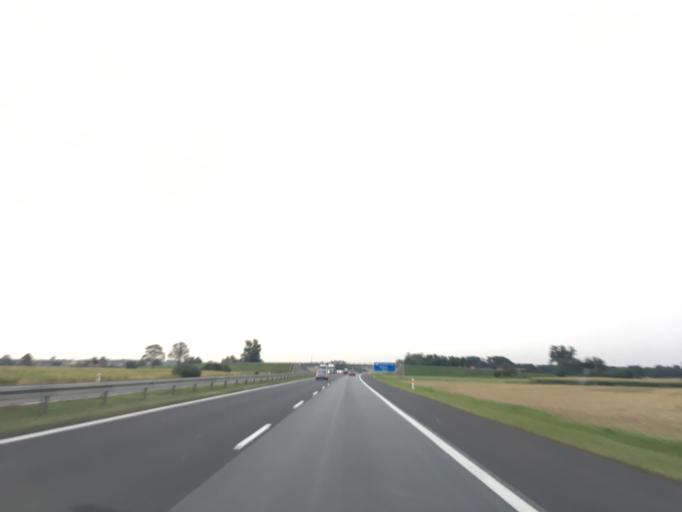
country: PL
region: Lodz Voivodeship
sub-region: Piotrkow Trybunalski
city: Piotrkow Trybunalski
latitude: 51.4600
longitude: 19.6382
